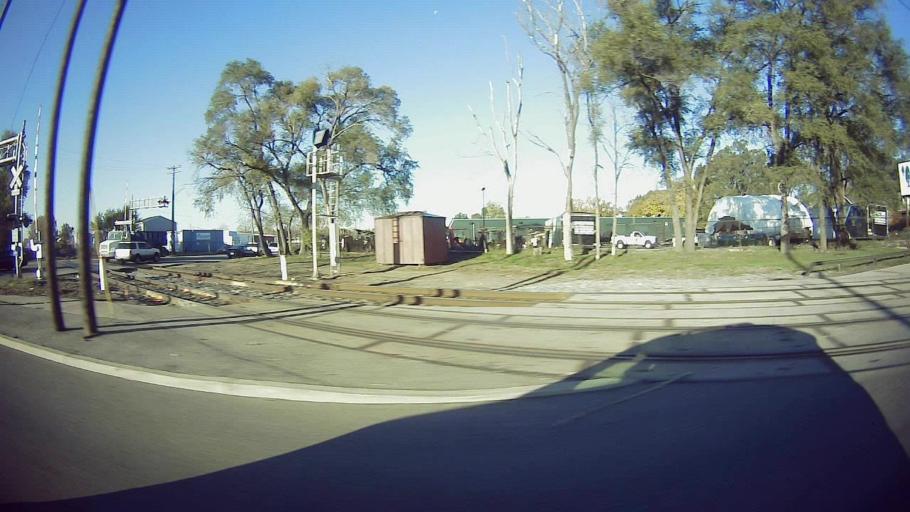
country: US
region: Michigan
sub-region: Wayne County
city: Hamtramck
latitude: 42.4242
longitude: -83.0241
